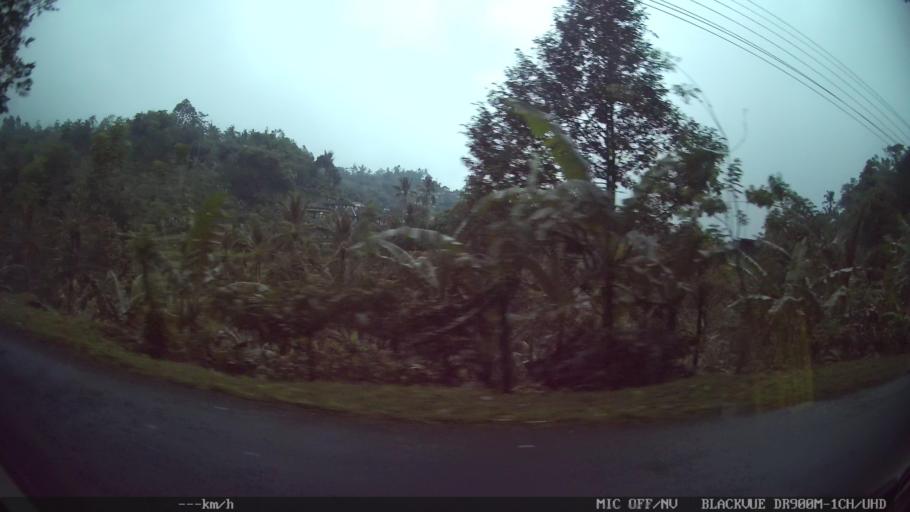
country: ID
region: Bali
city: Klau
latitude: -8.3637
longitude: 115.0310
